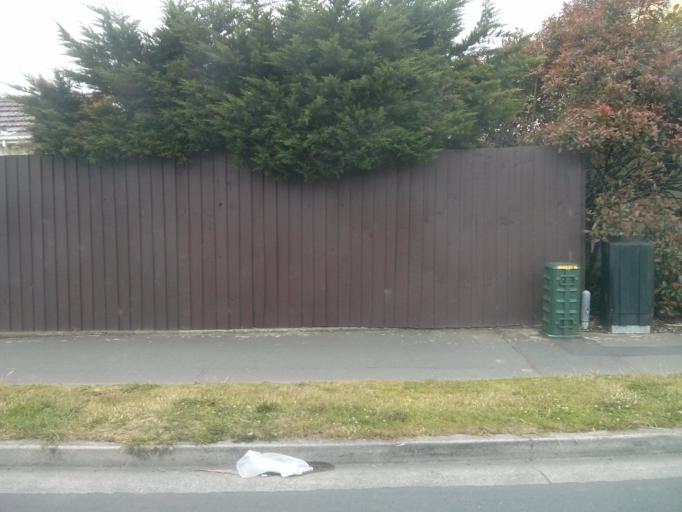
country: NZ
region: Canterbury
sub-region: Christchurch City
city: Christchurch
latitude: -43.5310
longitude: 172.5825
